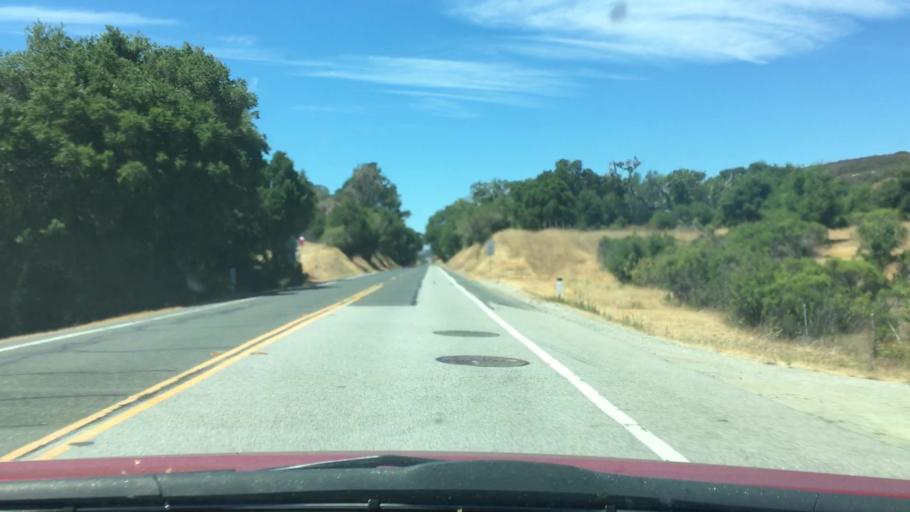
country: US
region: California
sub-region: San Mateo County
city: Emerald Lake Hills
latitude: 37.4663
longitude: -122.3002
